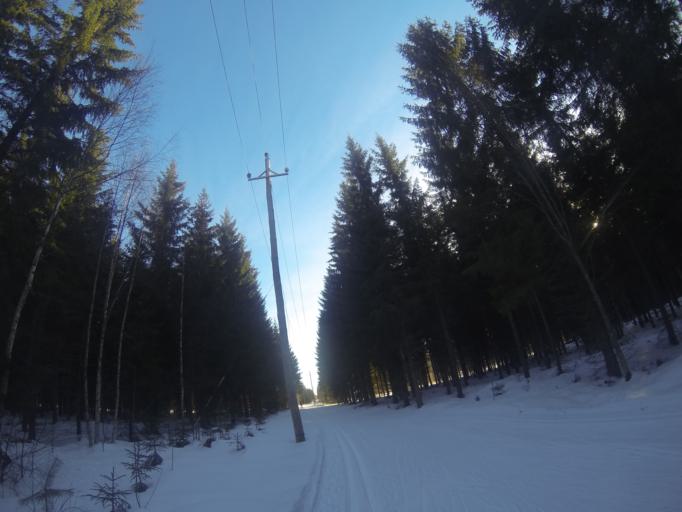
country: FI
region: Southern Savonia
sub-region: Savonlinna
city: Savonlinna
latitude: 61.9254
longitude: 28.8970
